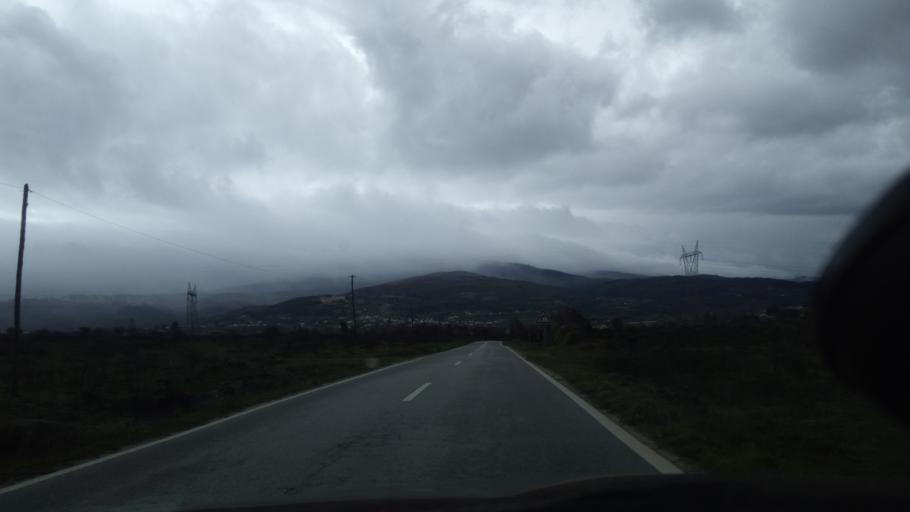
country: PT
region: Guarda
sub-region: Fornos de Algodres
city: Fornos de Algodres
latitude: 40.5513
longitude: -7.5688
